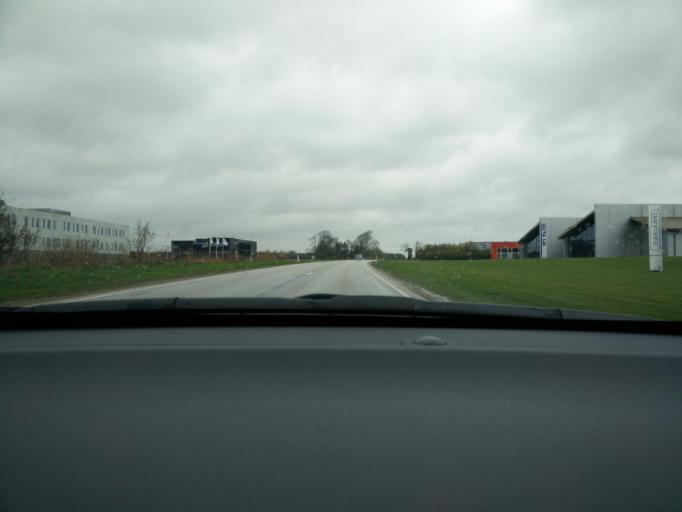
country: DK
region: Central Jutland
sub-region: Viborg Kommune
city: Viborg
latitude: 56.4633
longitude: 9.3734
